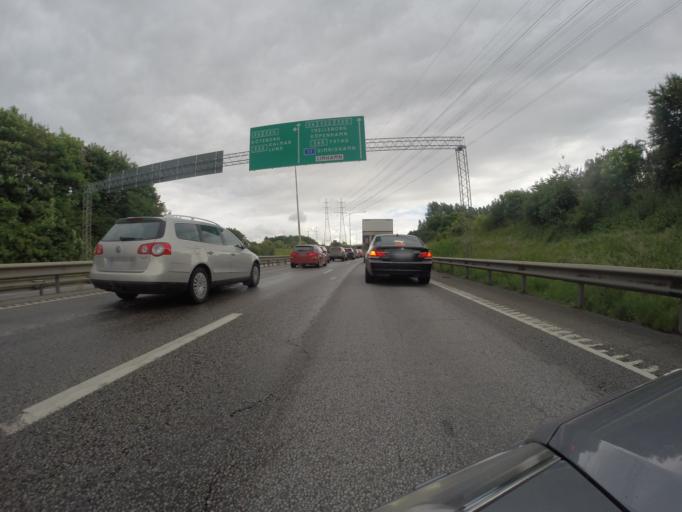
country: SE
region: Skane
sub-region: Burlovs Kommun
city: Arloev
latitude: 55.6245
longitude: 13.0563
